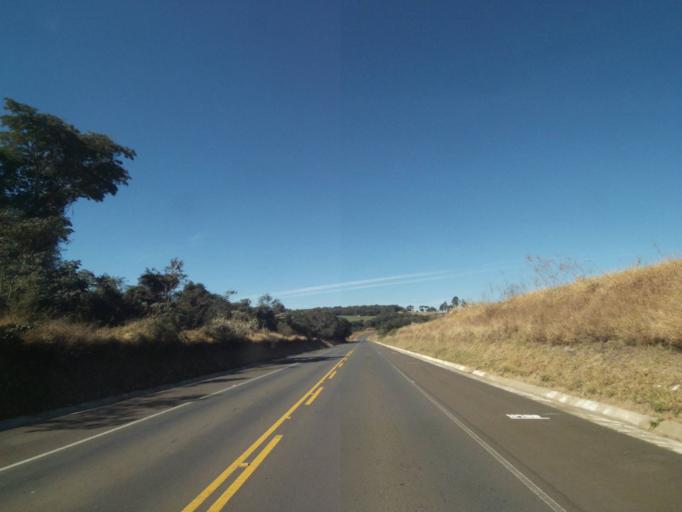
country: BR
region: Parana
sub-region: Tibagi
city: Tibagi
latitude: -24.7722
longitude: -50.4652
